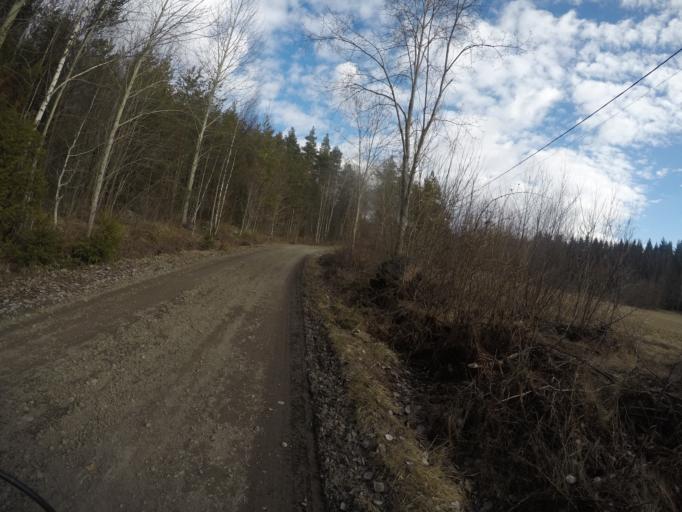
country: SE
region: Soedermanland
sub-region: Eskilstuna Kommun
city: Kvicksund
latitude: 59.4275
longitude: 16.2750
